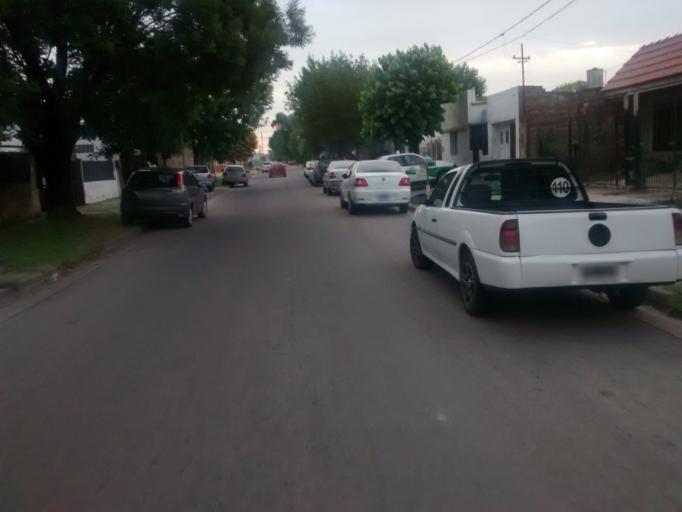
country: AR
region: Buenos Aires
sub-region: Partido de La Plata
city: La Plata
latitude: -34.9484
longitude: -57.9398
